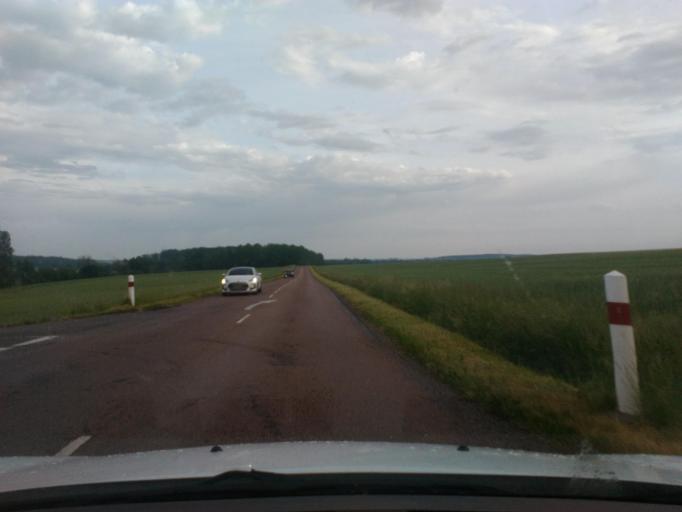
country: FR
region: Lorraine
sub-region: Departement des Vosges
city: Rambervillers
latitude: 48.4002
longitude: 6.5898
